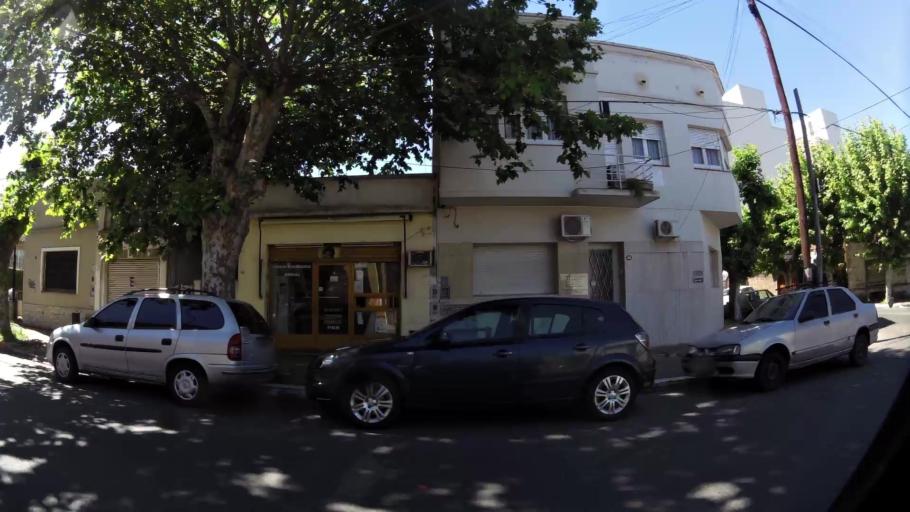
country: AR
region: Buenos Aires
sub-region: Partido de Quilmes
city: Quilmes
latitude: -34.7114
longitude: -58.2858
